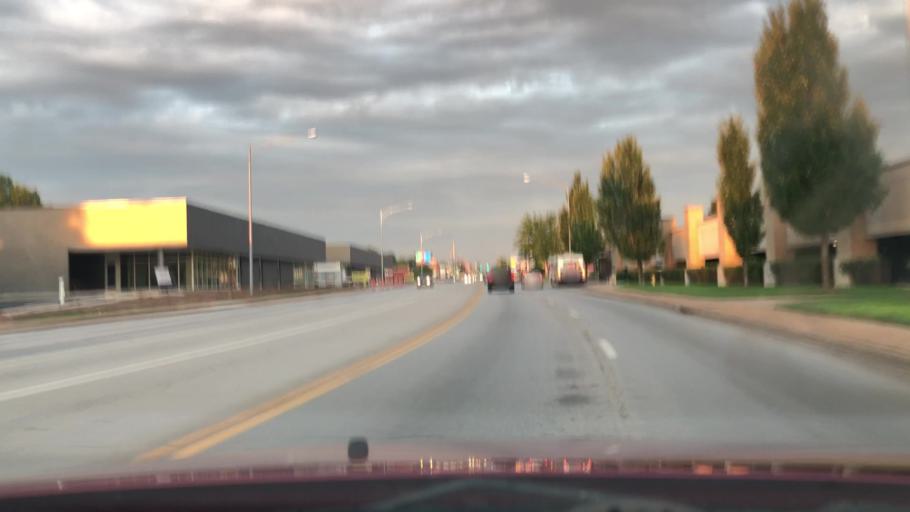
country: US
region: Missouri
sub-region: Greene County
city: Springfield
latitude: 37.1818
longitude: -93.2760
